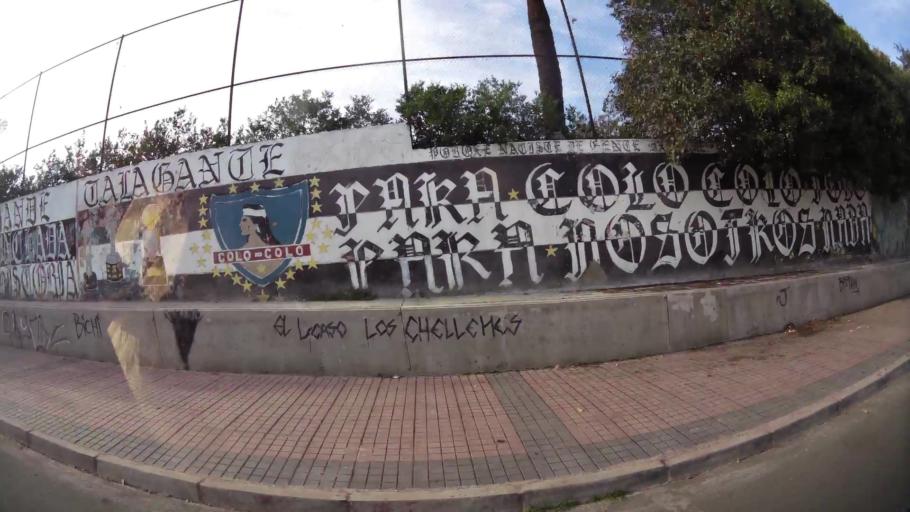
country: CL
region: Santiago Metropolitan
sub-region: Provincia de Talagante
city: Talagante
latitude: -33.6630
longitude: -70.9335
